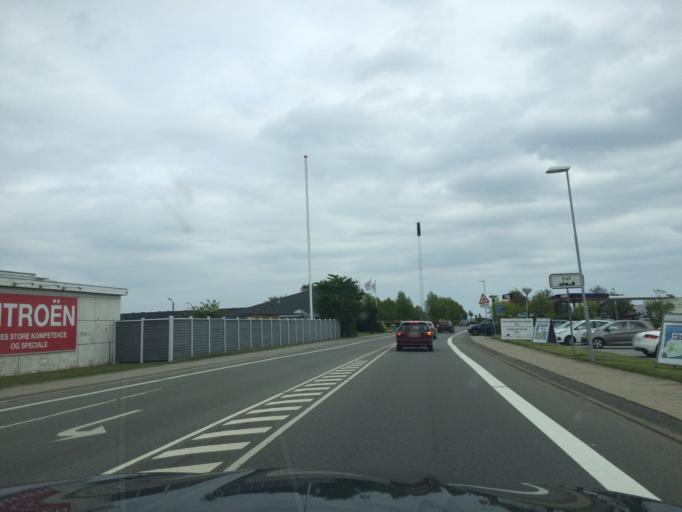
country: DK
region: Central Jutland
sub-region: Arhus Kommune
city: Hjortshoj
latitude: 56.2125
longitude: 10.2792
